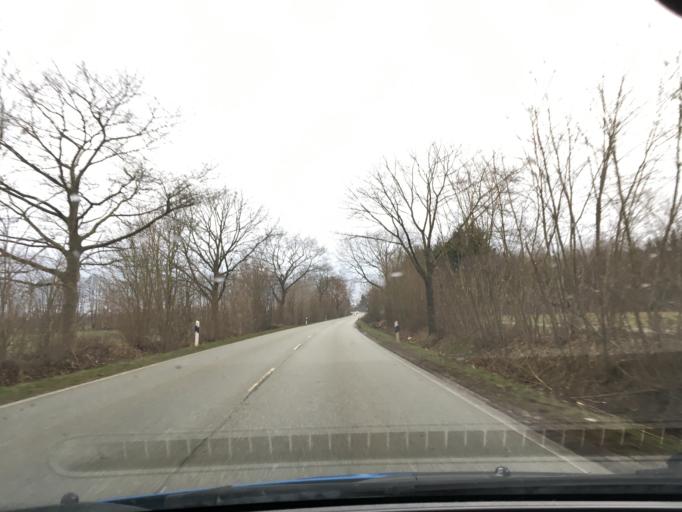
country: DE
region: Schleswig-Holstein
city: Siebeneichen
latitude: 53.4987
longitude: 10.6128
